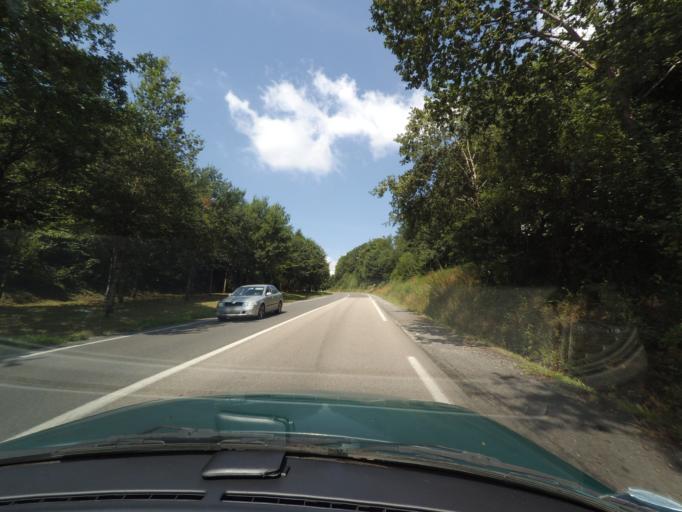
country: FR
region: Limousin
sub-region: Departement de la Haute-Vienne
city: Eymoutiers
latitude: 45.7386
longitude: 1.7324
